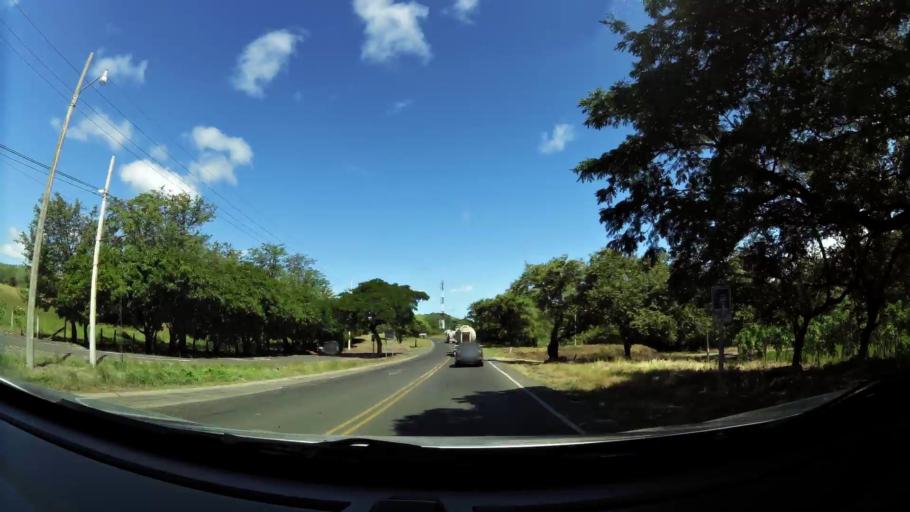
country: CR
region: Guanacaste
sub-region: Canton de Canas
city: Canas
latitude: 10.3916
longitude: -85.0807
